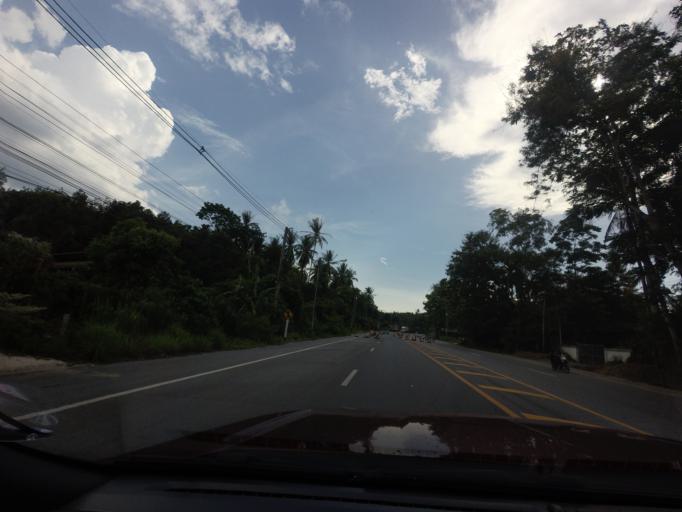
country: TH
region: Pattani
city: Khok Pho
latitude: 6.6772
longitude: 101.1394
